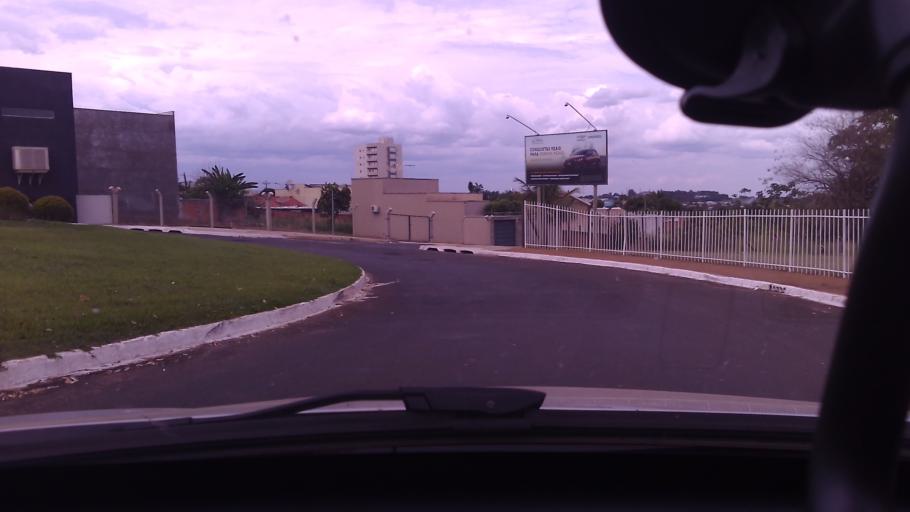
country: BR
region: Goias
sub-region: Mineiros
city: Mineiros
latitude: -17.5665
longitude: -52.5641
